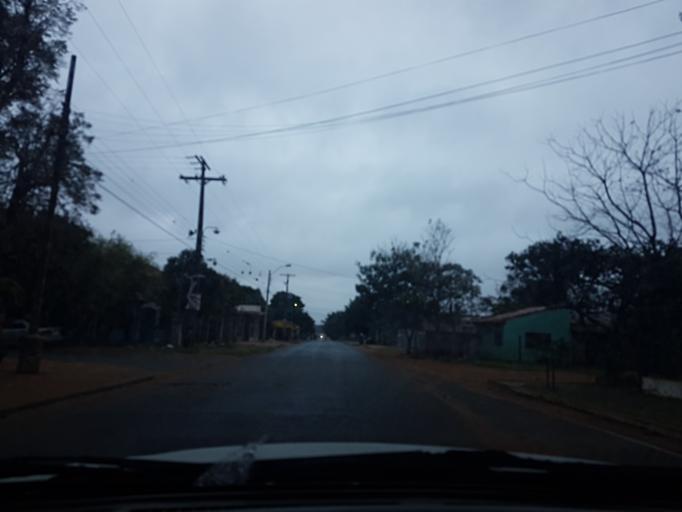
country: PY
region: Central
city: San Lorenzo
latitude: -25.2738
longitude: -57.4695
